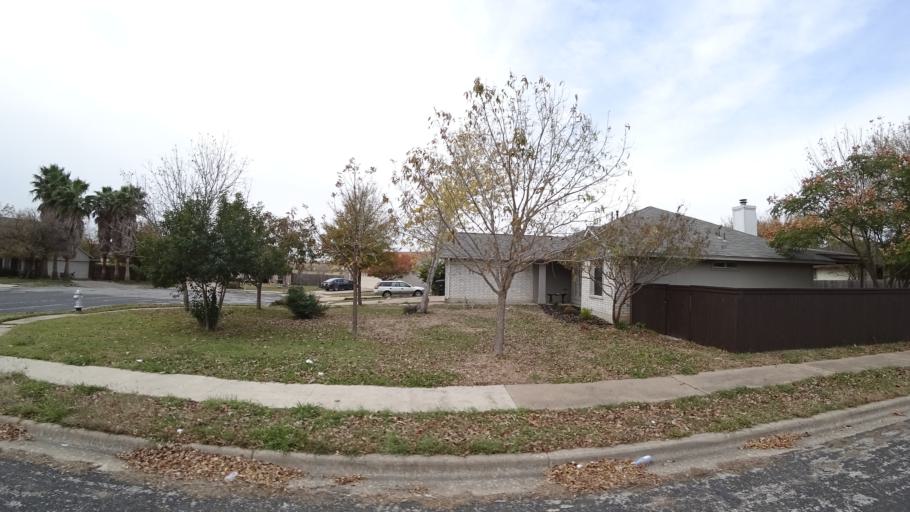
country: US
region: Texas
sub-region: Travis County
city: Garfield
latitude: 30.1578
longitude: -97.6492
